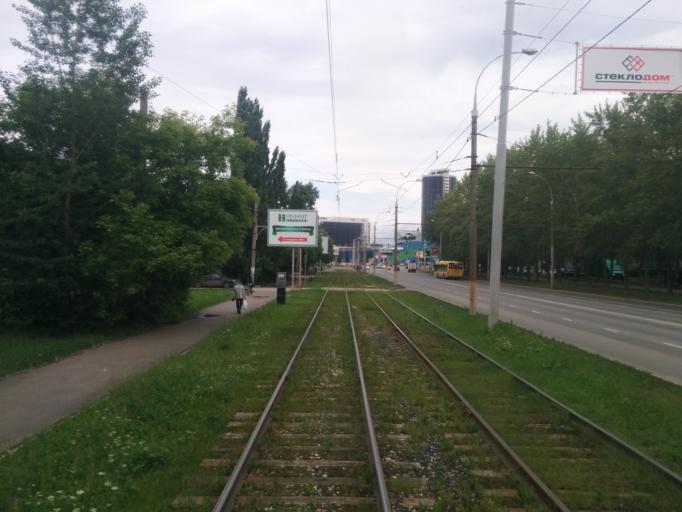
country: RU
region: Perm
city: Perm
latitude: 58.0018
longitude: 56.2865
